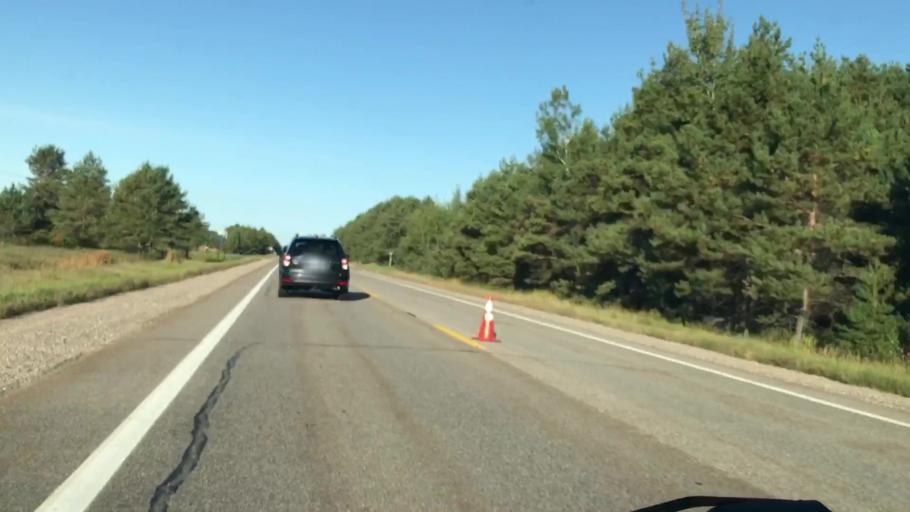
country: US
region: Michigan
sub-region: Chippewa County
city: Sault Ste. Marie
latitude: 46.3755
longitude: -84.6116
